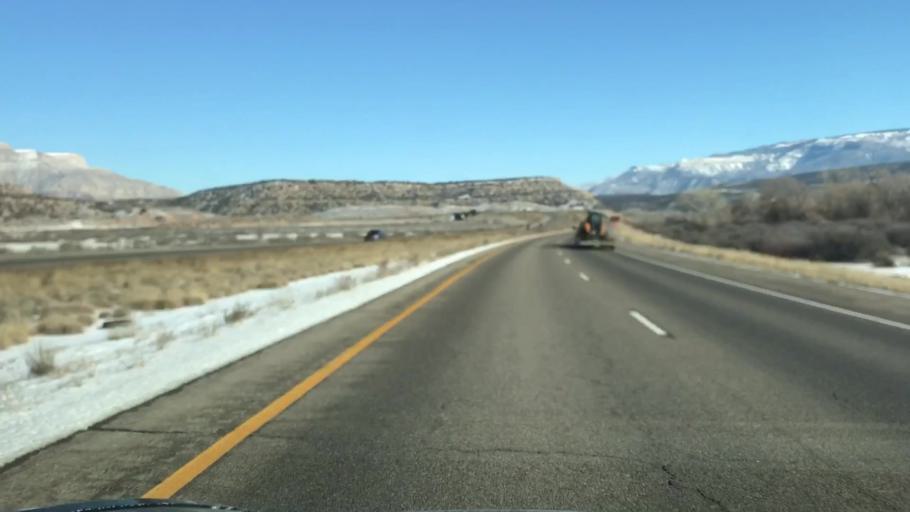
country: US
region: Colorado
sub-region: Garfield County
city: Parachute
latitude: 39.3506
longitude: -108.1806
